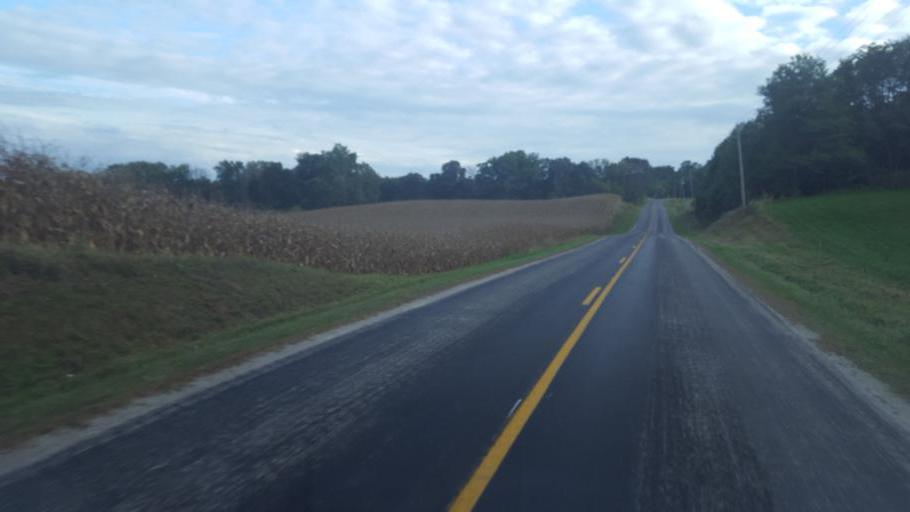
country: US
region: Ohio
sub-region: Ashland County
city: Loudonville
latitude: 40.7068
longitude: -82.1694
